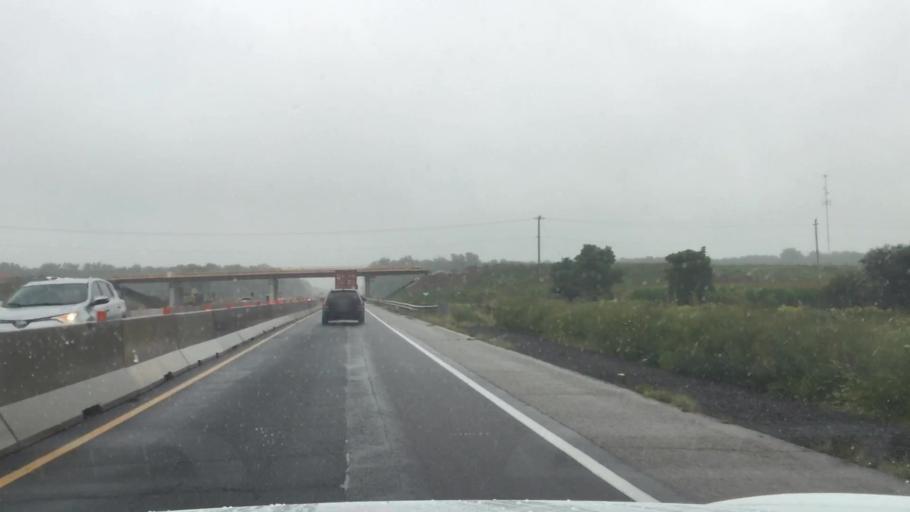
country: CA
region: Ontario
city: Delaware
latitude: 42.7935
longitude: -81.3491
